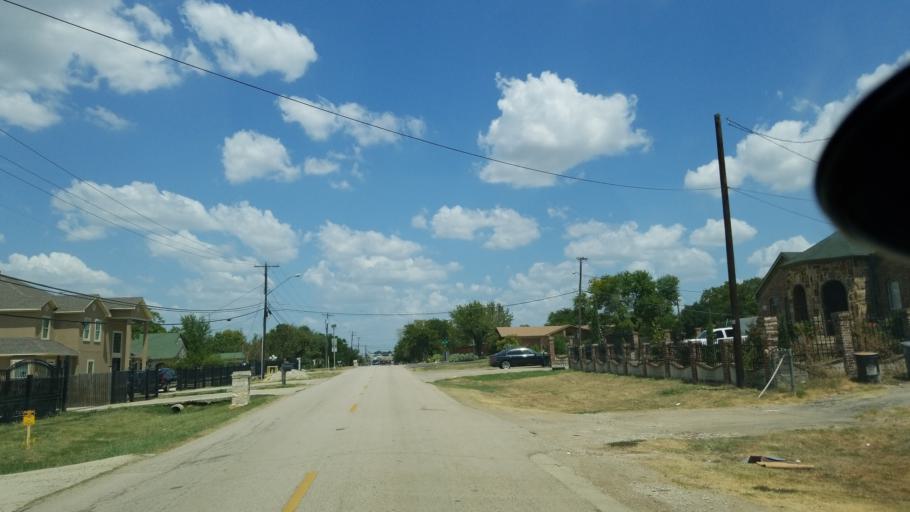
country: US
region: Texas
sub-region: Dallas County
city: Cockrell Hill
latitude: 32.7451
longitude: -96.9255
